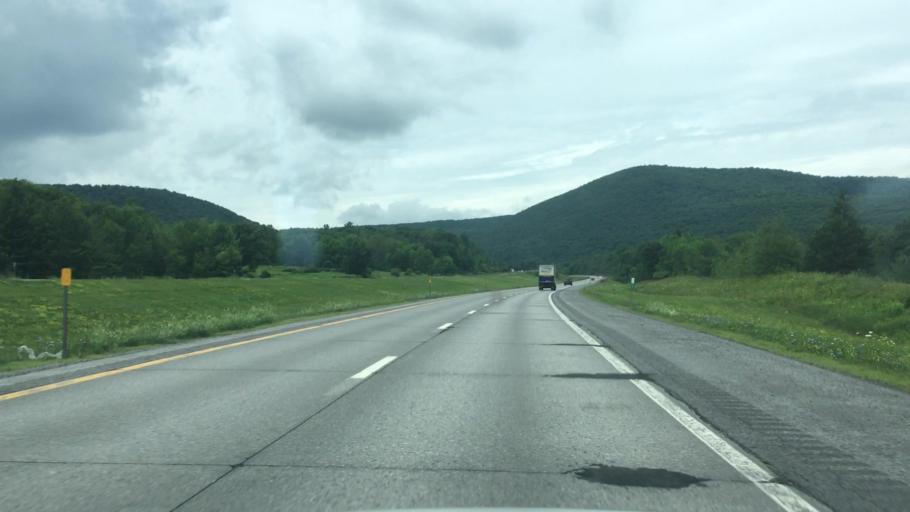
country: US
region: New York
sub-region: Schoharie County
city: Cobleskill
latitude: 42.6489
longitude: -74.6165
